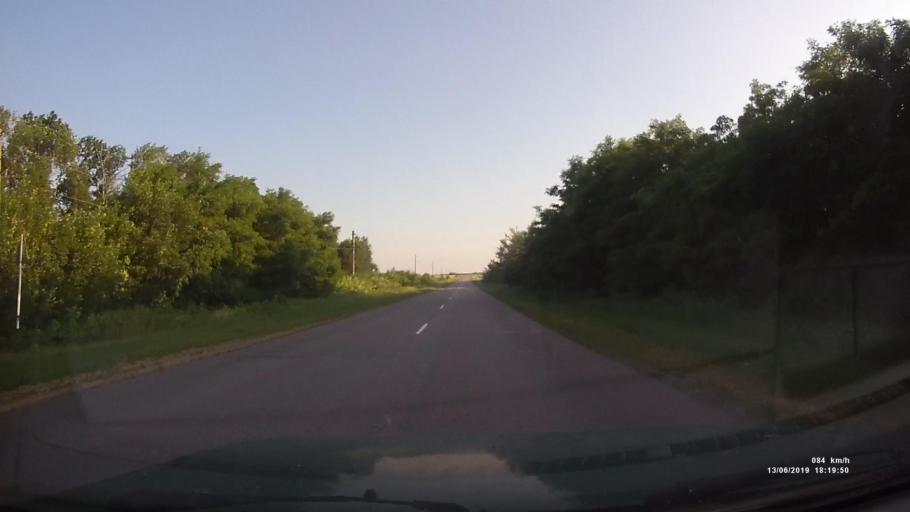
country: RU
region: Rostov
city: Kazanskaya
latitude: 49.8913
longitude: 41.3037
